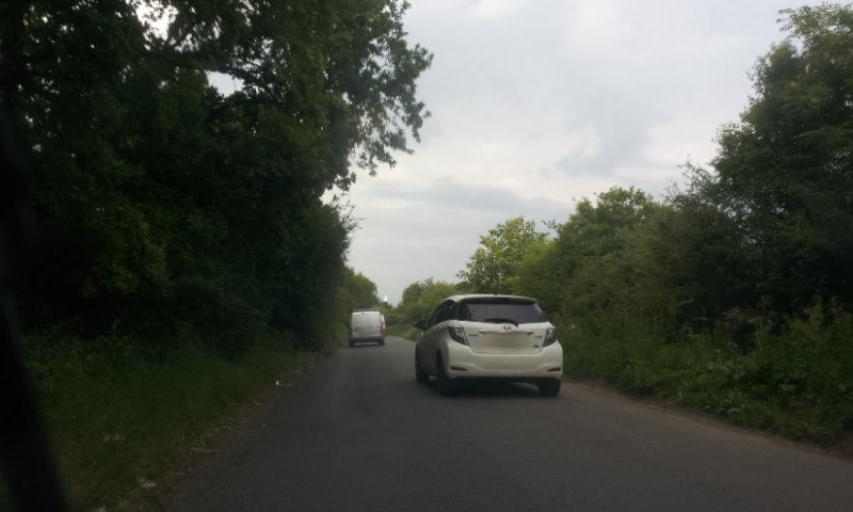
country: GB
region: England
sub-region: Kent
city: Paddock Wood
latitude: 51.1875
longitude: 0.4182
